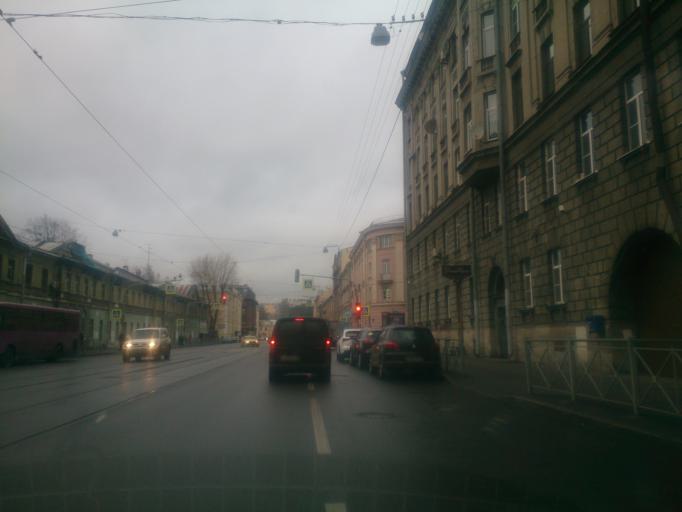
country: RU
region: St.-Petersburg
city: Centralniy
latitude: 59.9205
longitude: 30.3388
